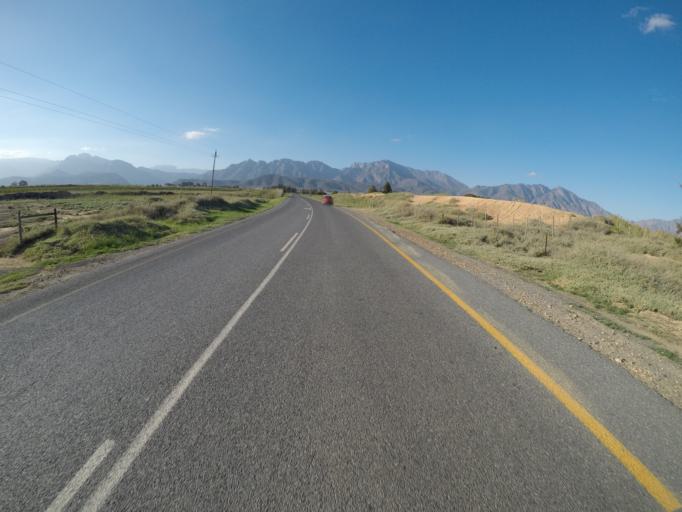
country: ZA
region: Western Cape
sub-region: Cape Winelands District Municipality
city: Worcester
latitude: -33.6701
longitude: 19.5425
